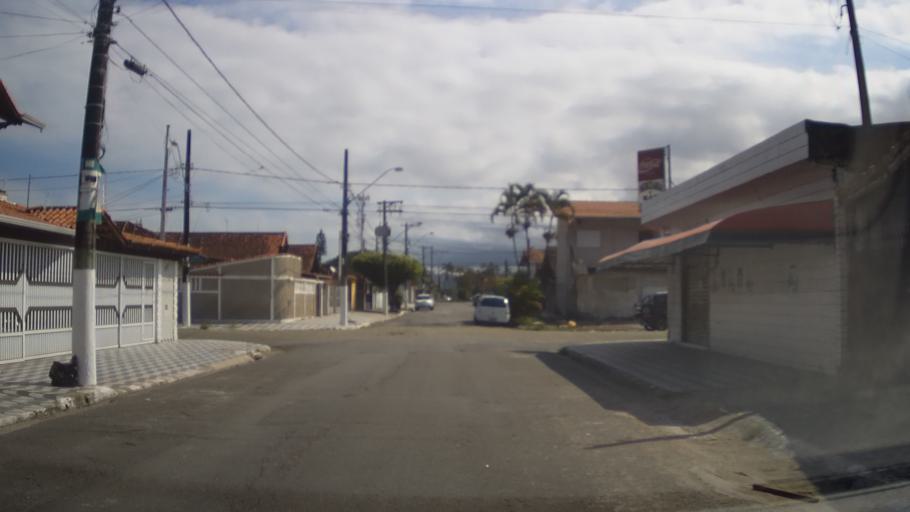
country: BR
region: Sao Paulo
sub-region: Praia Grande
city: Praia Grande
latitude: -24.0188
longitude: -46.4657
